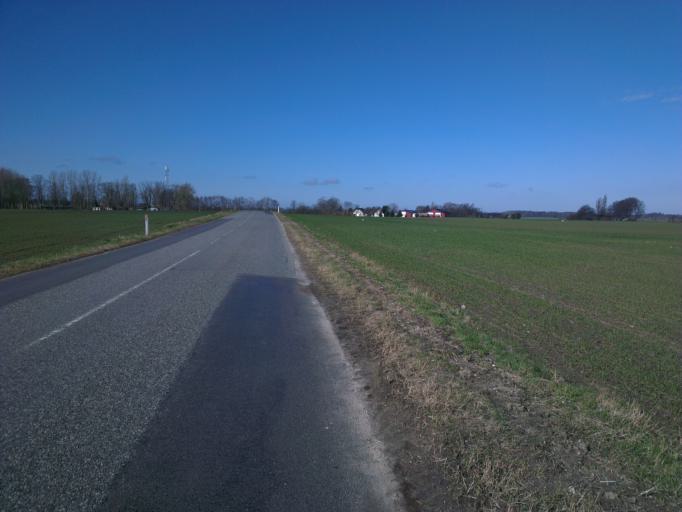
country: DK
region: Capital Region
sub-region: Hillerod Kommune
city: Skaevinge
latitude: 55.8829
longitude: 12.1172
